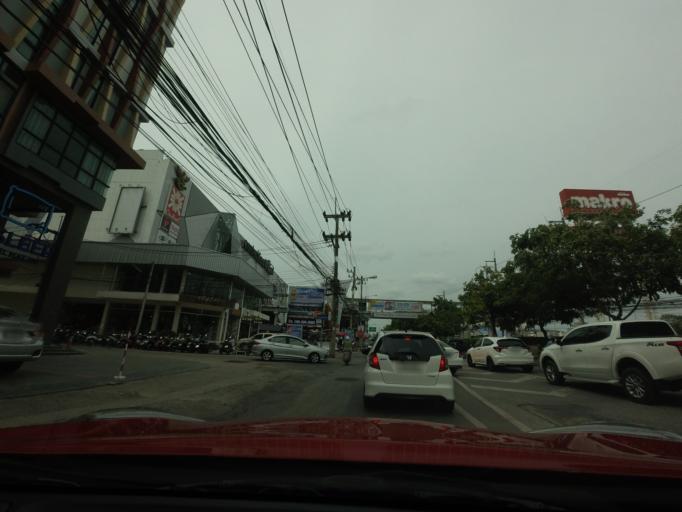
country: TH
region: Songkhla
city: Hat Yai
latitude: 6.9902
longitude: 100.4840
